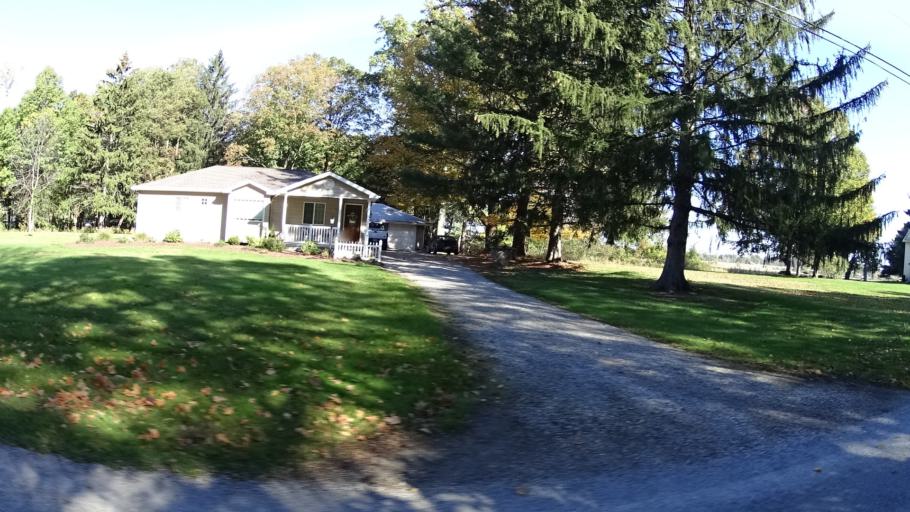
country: US
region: Ohio
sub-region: Lorain County
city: Vermilion-on-the-Lake
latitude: 41.3985
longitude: -82.2908
